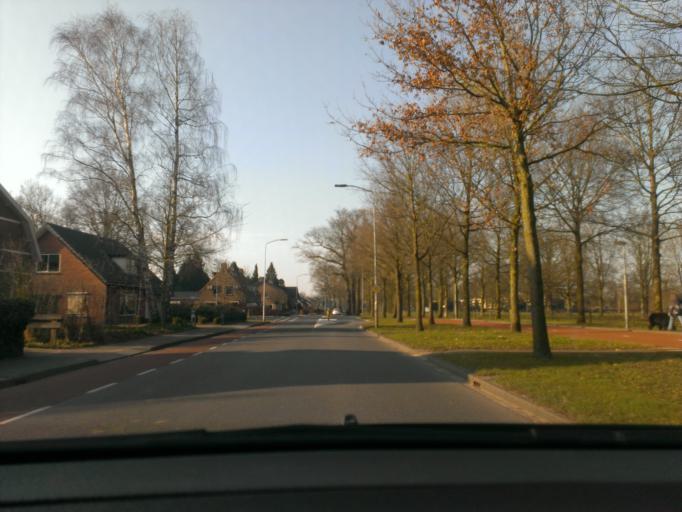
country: NL
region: Gelderland
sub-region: Gemeente Voorst
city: Twello
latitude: 52.2334
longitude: 6.1102
